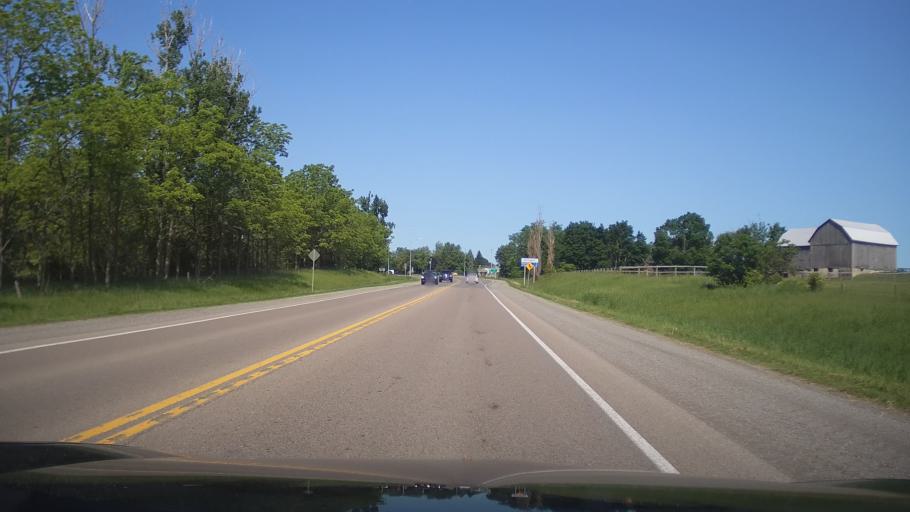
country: CA
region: Ontario
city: Omemee
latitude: 44.3476
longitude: -78.8009
